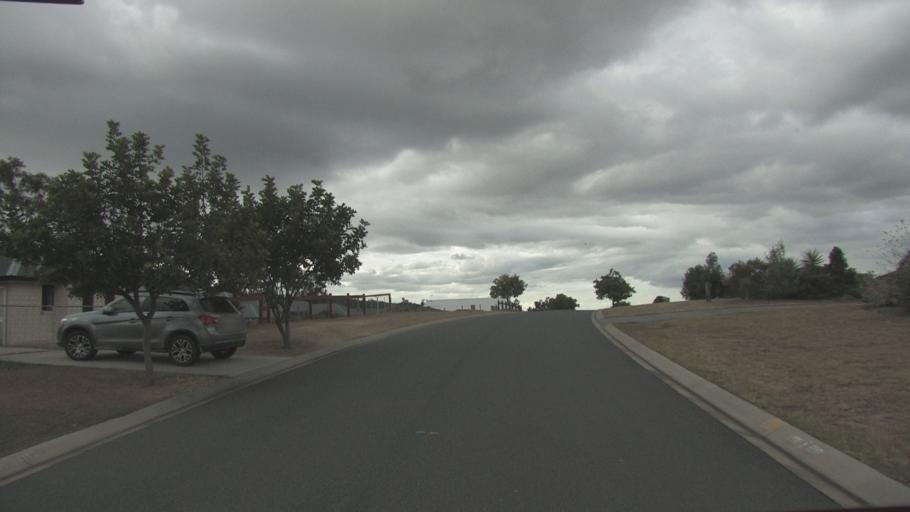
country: AU
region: Queensland
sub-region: Logan
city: Cedar Vale
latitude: -27.8647
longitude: 153.0762
